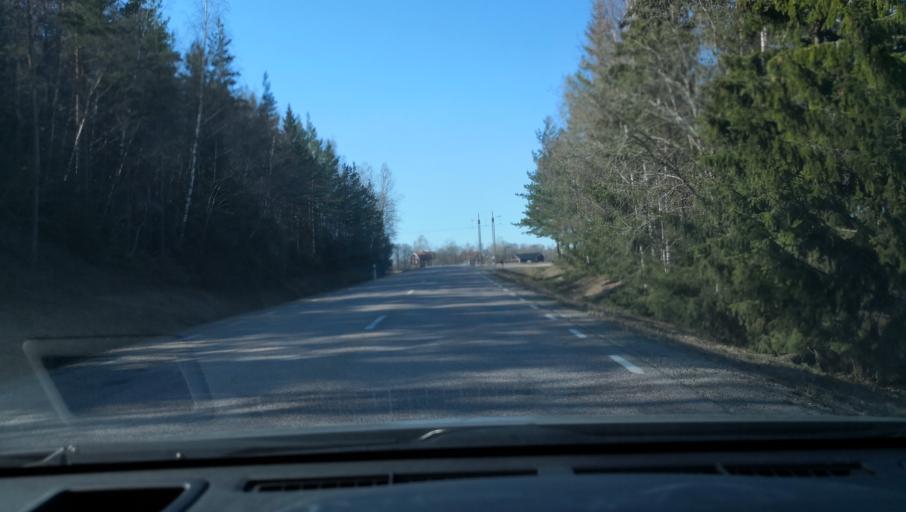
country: SE
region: Vaestmanland
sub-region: Sala Kommun
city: Sala
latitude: 59.9106
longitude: 16.5251
